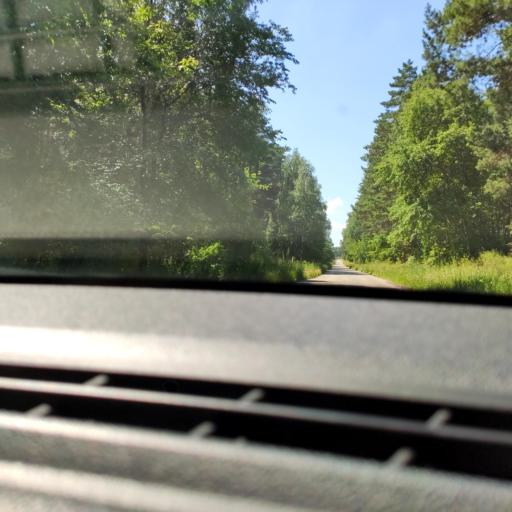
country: RU
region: Samara
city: Podstepki
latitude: 53.5700
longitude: 49.0266
